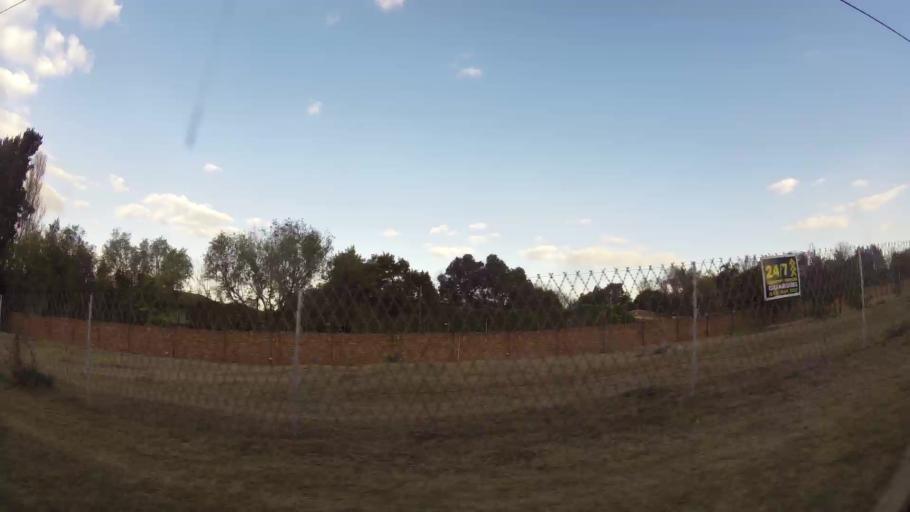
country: ZA
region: Gauteng
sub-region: City of Johannesburg Metropolitan Municipality
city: Diepsloot
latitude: -25.9991
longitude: 28.0037
